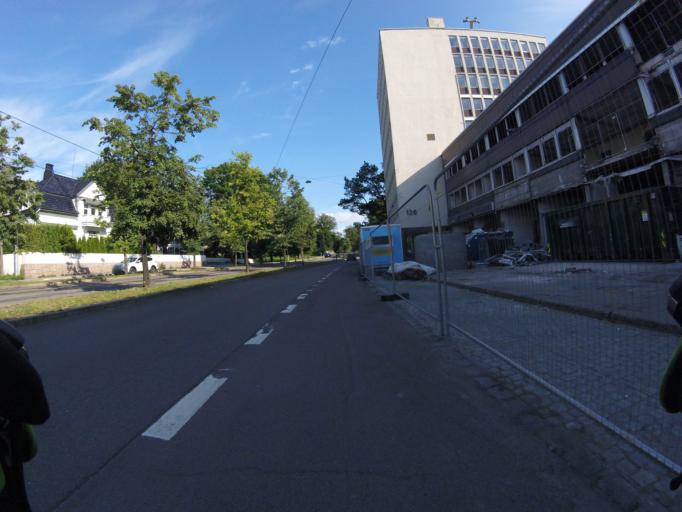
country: NO
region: Oslo
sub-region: Oslo
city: Sjolyststranda
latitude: 59.9214
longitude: 10.6887
